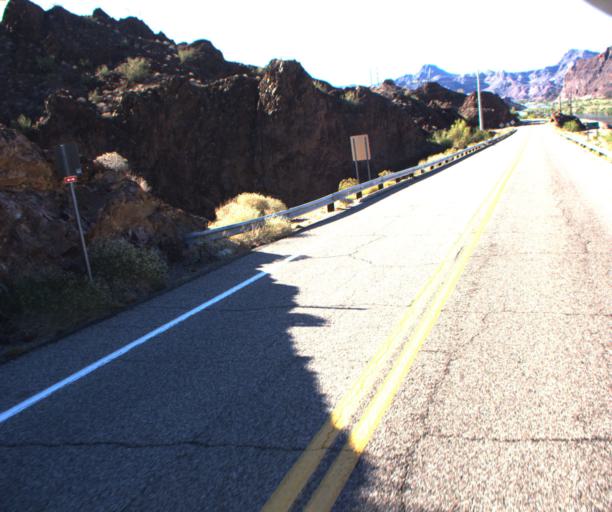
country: US
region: Arizona
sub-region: La Paz County
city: Cienega Springs
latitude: 34.2942
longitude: -114.1379
